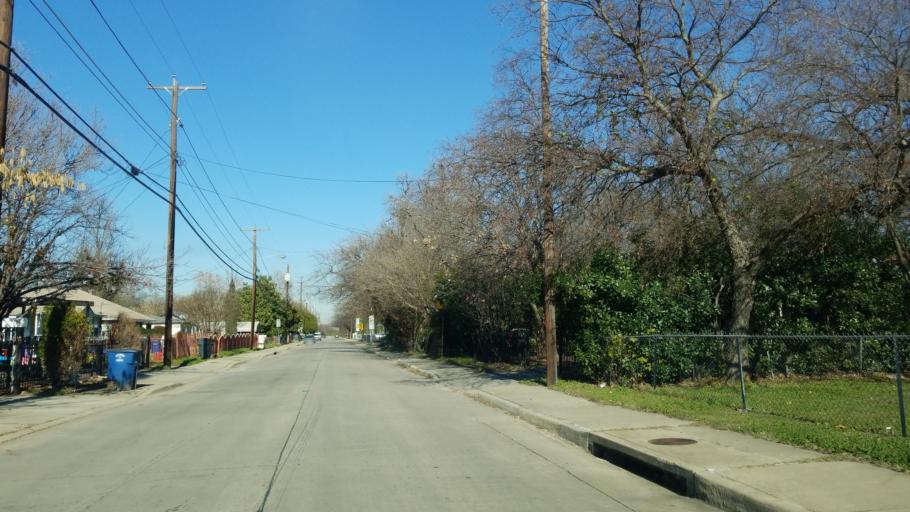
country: US
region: Texas
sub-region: Dallas County
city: Cockrell Hill
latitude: 32.7549
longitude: -96.9114
